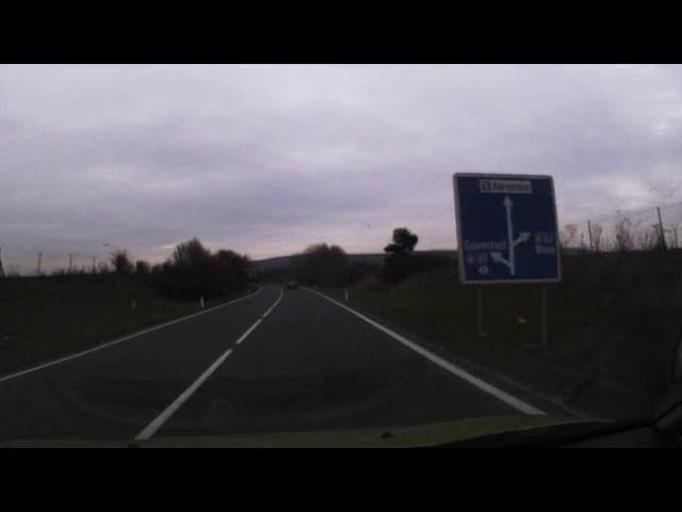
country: AT
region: Burgenland
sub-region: Eisenstadt-Umgebung
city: Steinbrunn
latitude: 47.8649
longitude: 16.4142
